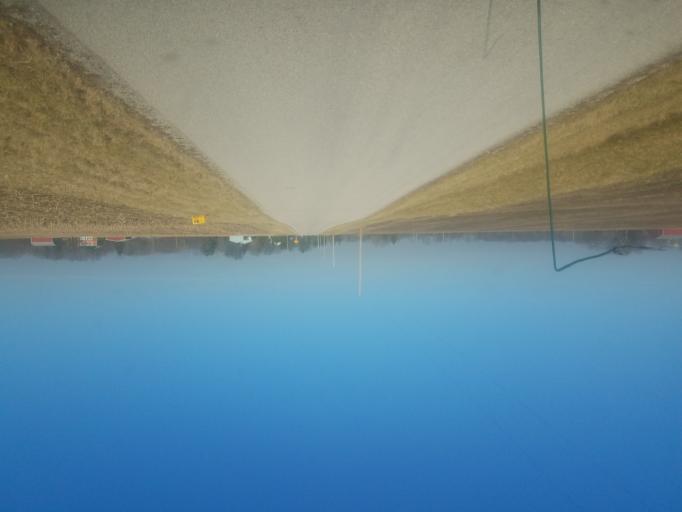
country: US
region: Ohio
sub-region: Seneca County
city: Tiffin
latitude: 41.1208
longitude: -83.1120
